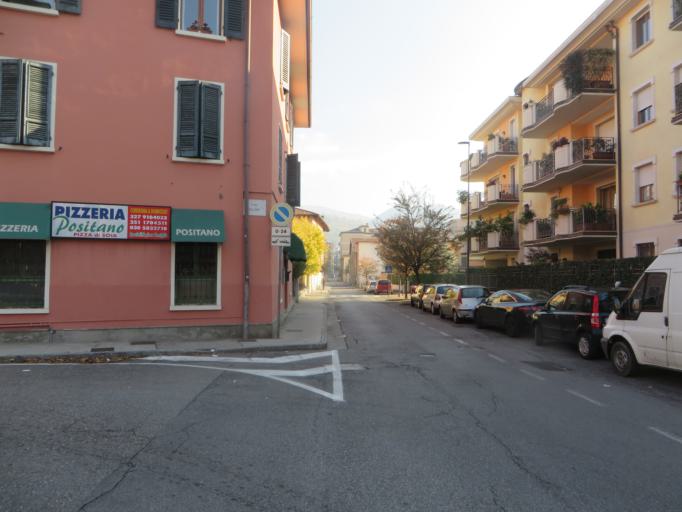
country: IT
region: Lombardy
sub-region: Provincia di Brescia
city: Brescia
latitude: 45.5525
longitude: 10.2203
